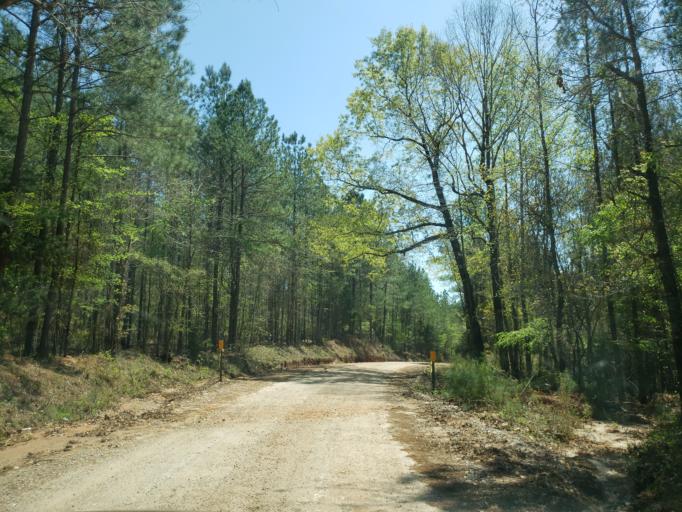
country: US
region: Alabama
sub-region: Lee County
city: Auburn
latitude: 32.6352
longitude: -85.6417
